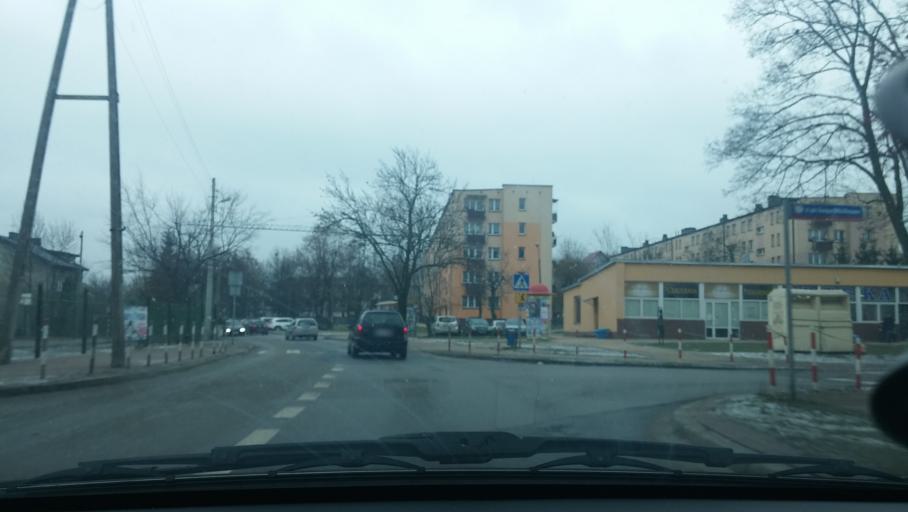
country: PL
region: Masovian Voivodeship
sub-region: Siedlce
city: Siedlce
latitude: 52.1617
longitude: 22.2664
